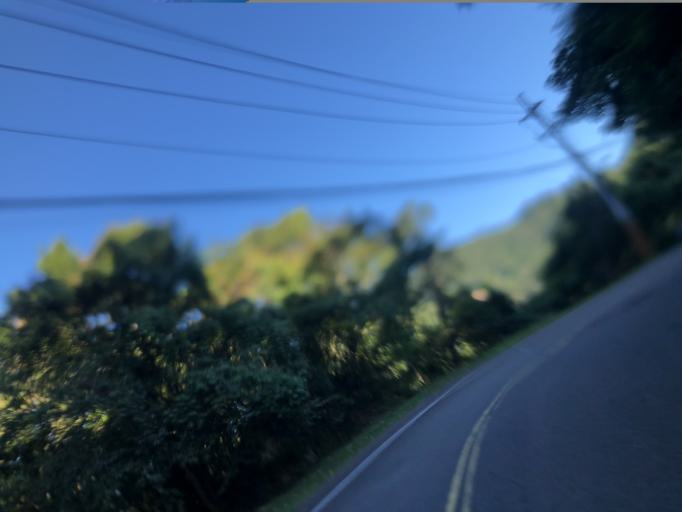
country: TW
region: Taiwan
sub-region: Miaoli
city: Miaoli
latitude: 24.5817
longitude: 120.9297
